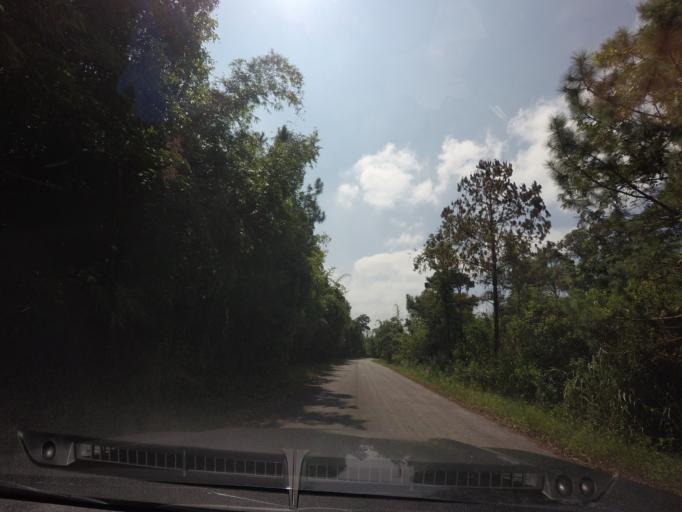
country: TH
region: Loei
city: Na Haeo
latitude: 17.4959
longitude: 100.9388
